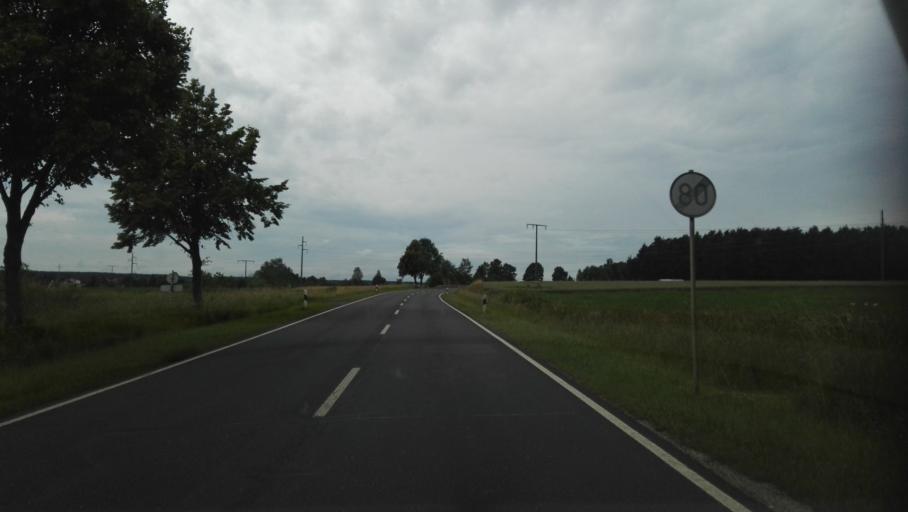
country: DE
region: Bavaria
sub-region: Upper Franconia
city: Plankenfels
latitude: 49.9004
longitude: 11.3304
